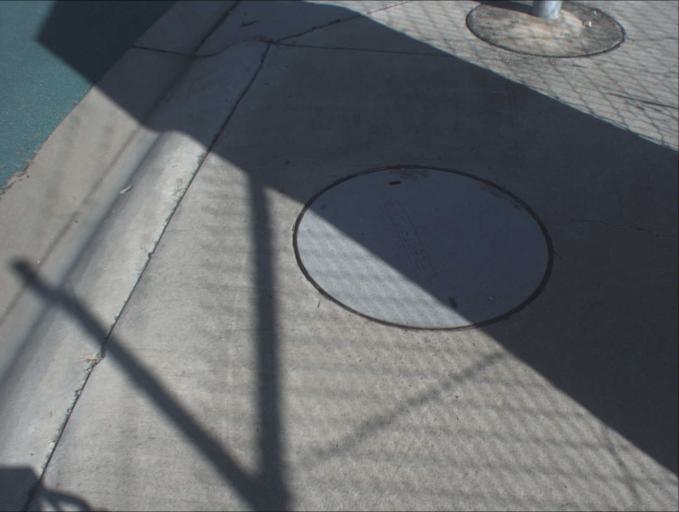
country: AU
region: Queensland
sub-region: Logan
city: Waterford West
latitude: -27.7021
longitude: 153.1568
